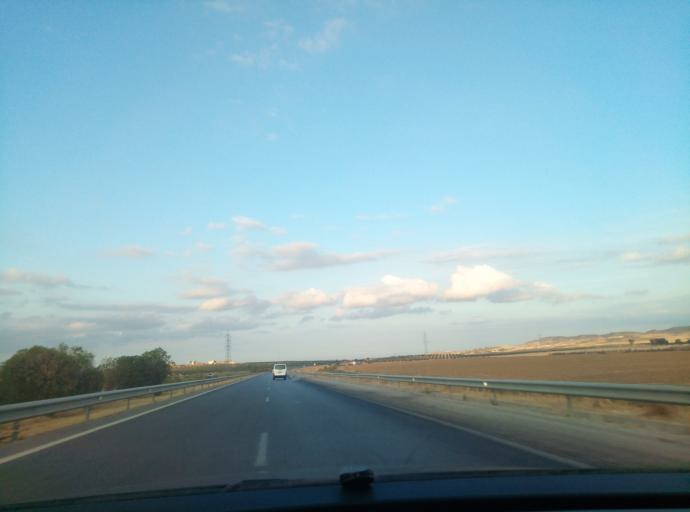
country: TN
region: Manouba
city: El Battan
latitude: 36.6643
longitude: 9.8560
